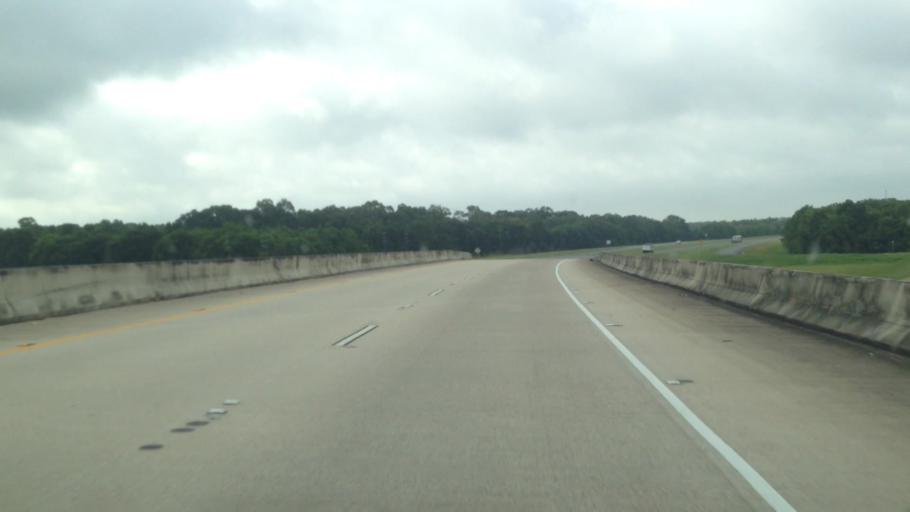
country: US
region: Louisiana
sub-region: Saint Landry Parish
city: Opelousas
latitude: 30.6424
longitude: -92.0503
